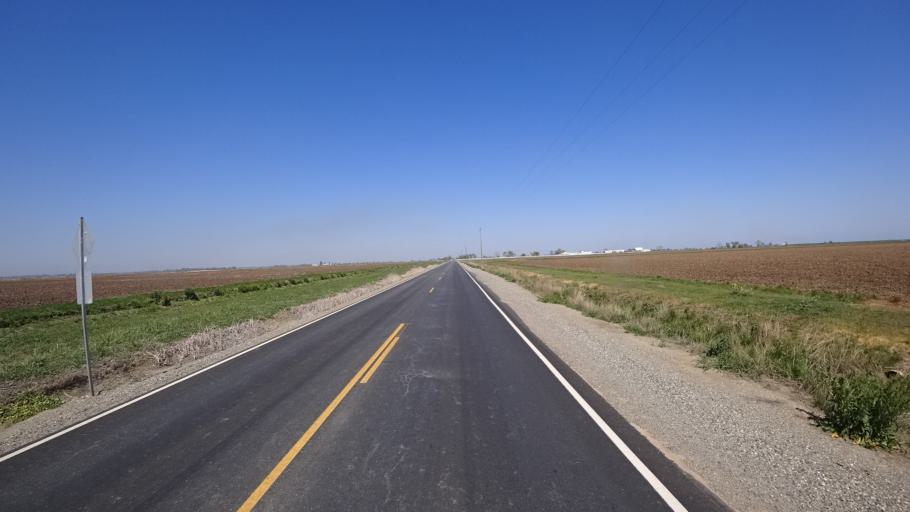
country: US
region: California
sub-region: Glenn County
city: Willows
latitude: 39.4959
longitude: -122.1367
